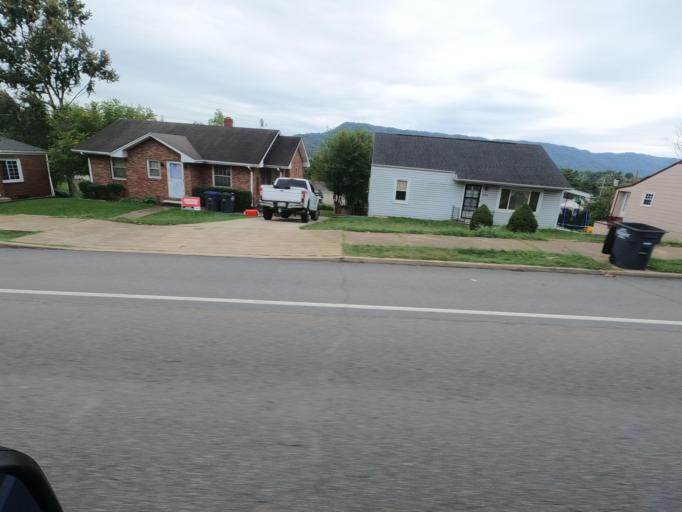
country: US
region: Tennessee
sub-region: Sullivan County
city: Kingsport
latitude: 36.5556
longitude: -82.5877
